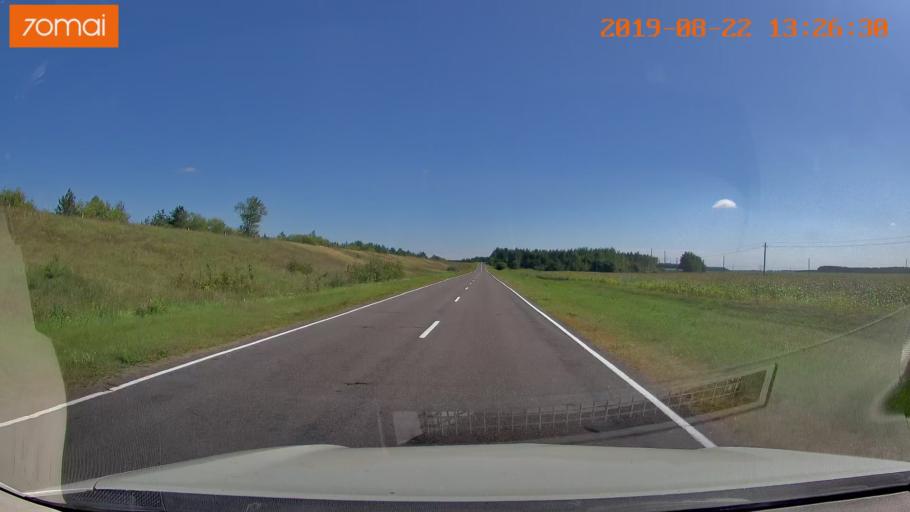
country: BY
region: Minsk
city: Staryya Darohi
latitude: 53.2093
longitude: 28.0637
